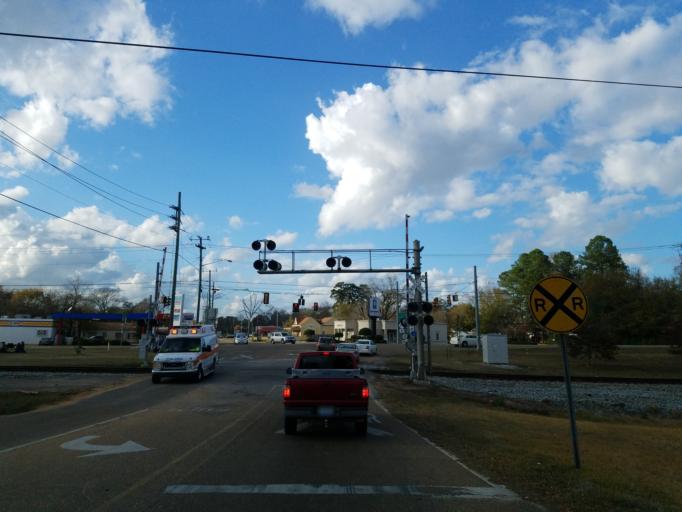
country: US
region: Mississippi
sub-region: Jones County
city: Ellisville
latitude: 31.6054
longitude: -89.1964
